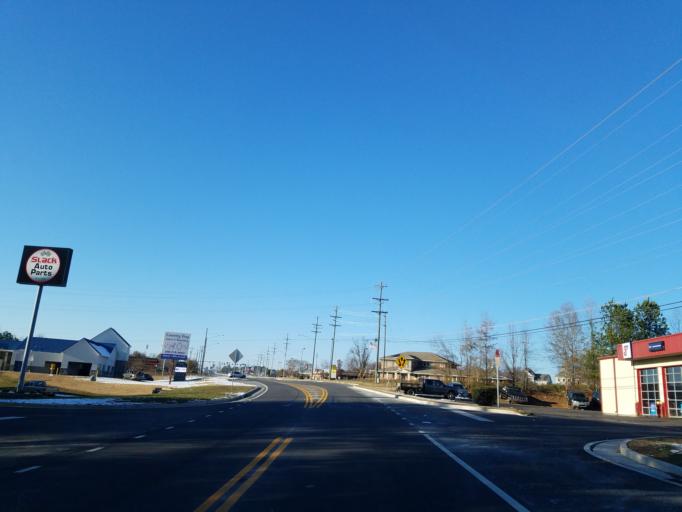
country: US
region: Georgia
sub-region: Dawson County
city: Dawsonville
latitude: 34.3597
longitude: -84.0327
